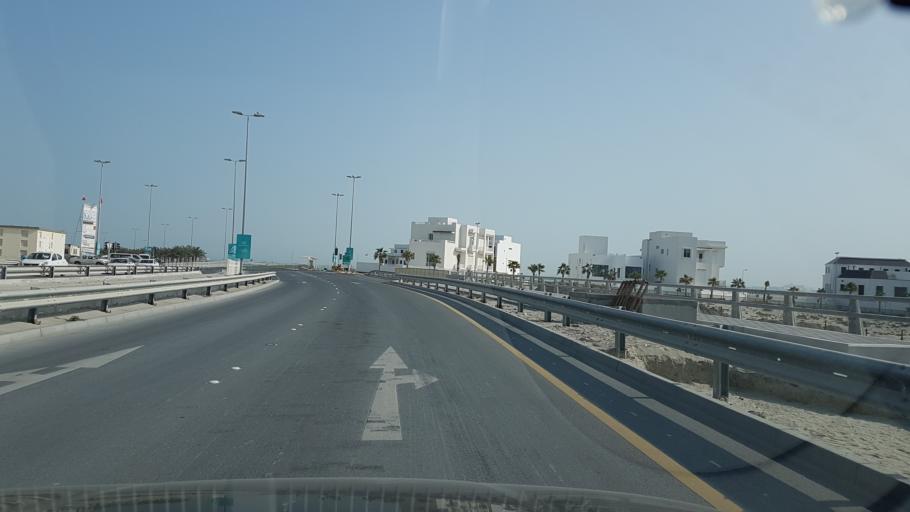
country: BH
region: Muharraq
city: Al Hadd
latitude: 26.2697
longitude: 50.6703
